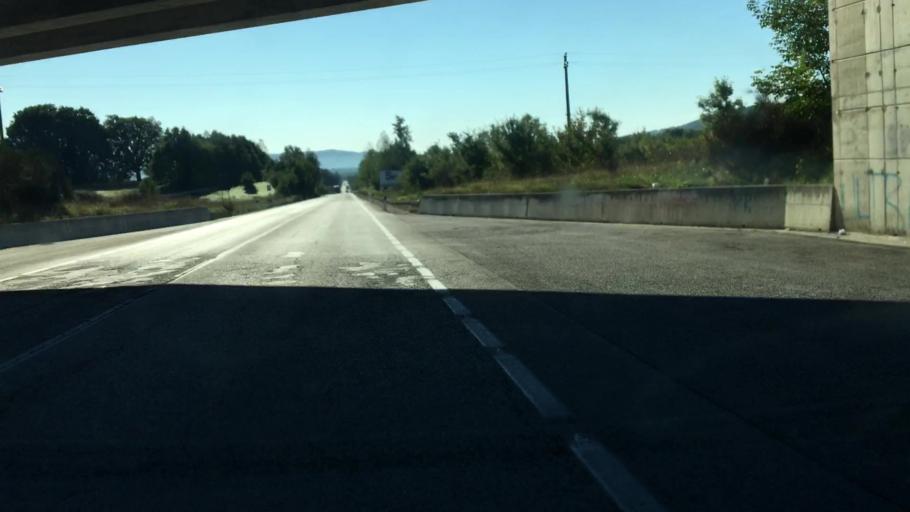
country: IT
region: Molise
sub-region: Provincia di Campobasso
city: Vinchiaturo
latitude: 41.4522
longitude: 14.5866
